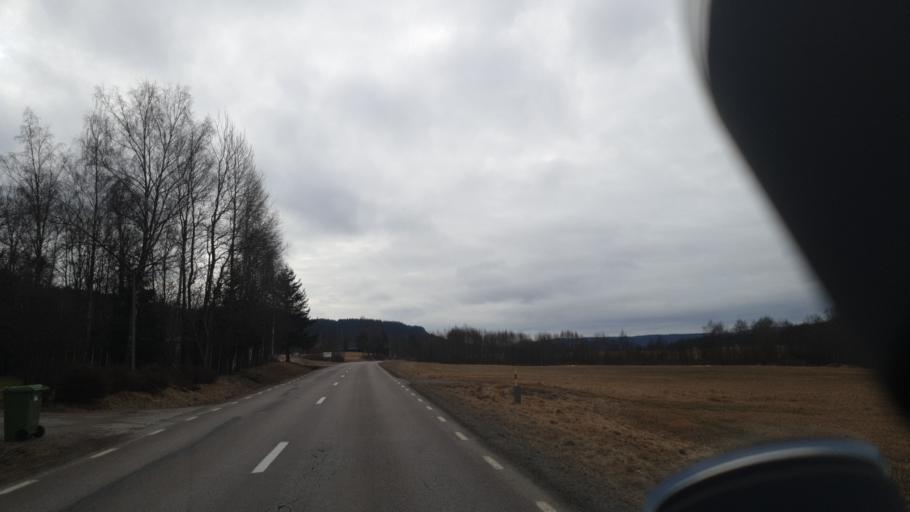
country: SE
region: Vaermland
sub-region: Eda Kommun
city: Amotfors
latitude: 59.6690
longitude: 12.1457
